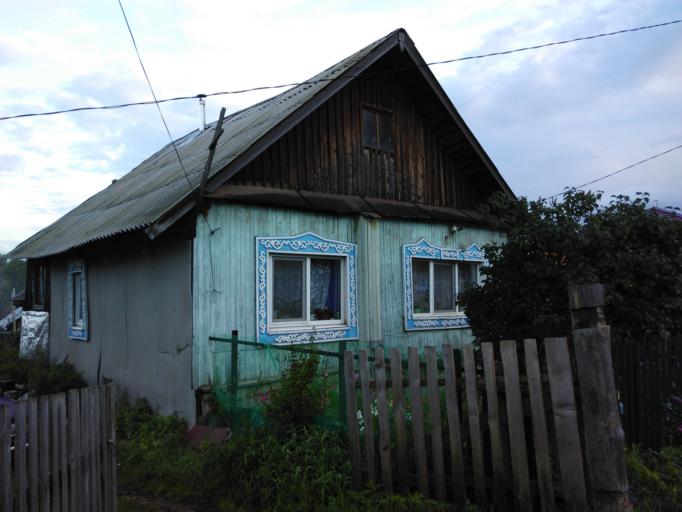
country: RU
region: Perm
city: Foki
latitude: 56.6935
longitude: 54.3495
